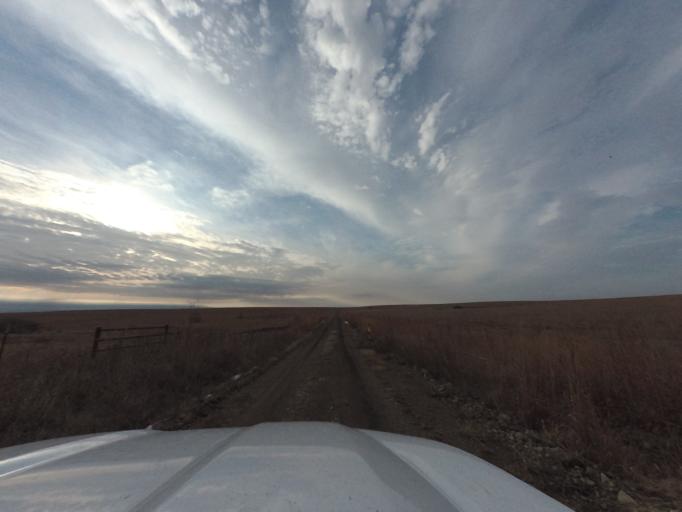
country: US
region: Kansas
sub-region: Chase County
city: Cottonwood Falls
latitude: 38.4684
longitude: -96.4471
